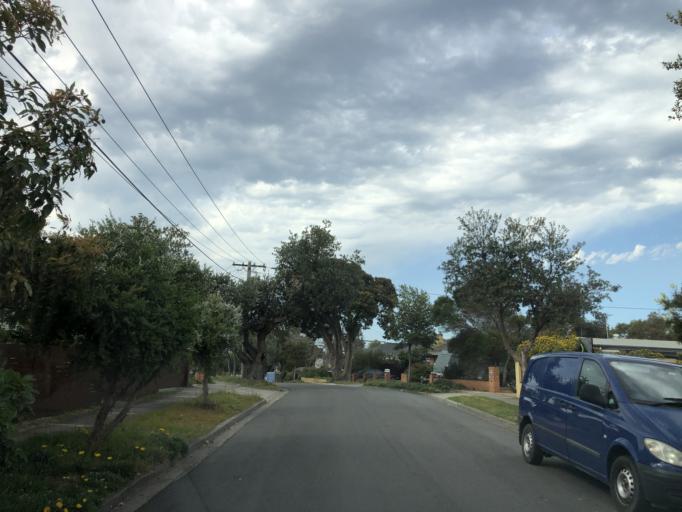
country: AU
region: Victoria
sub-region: Kingston
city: Carrum
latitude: -38.0827
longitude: 145.1254
